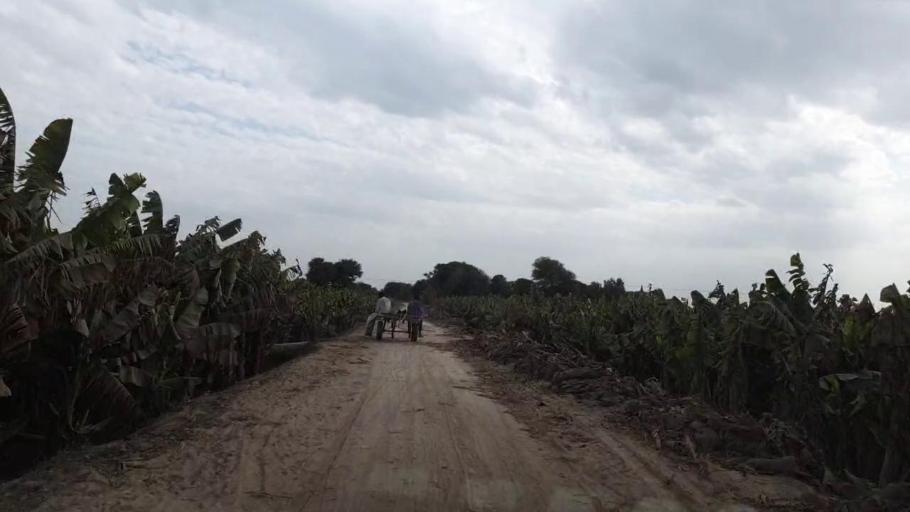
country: PK
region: Sindh
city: Tando Jam
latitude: 25.5473
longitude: 68.5731
